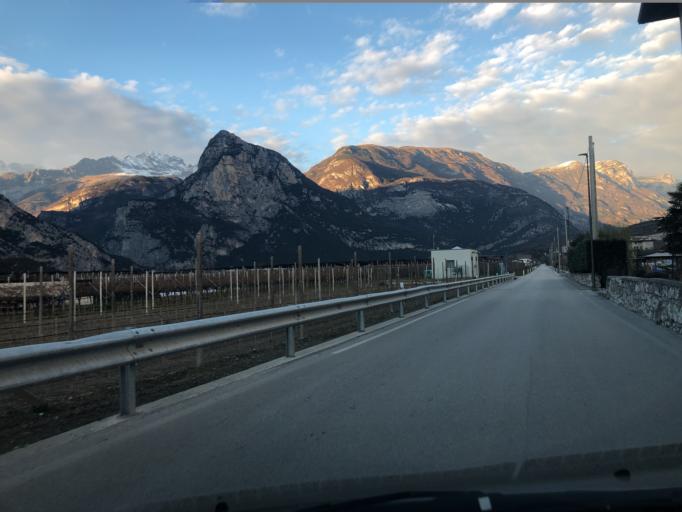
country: IT
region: Trentino-Alto Adige
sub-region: Provincia di Trento
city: Pietramurata
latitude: 46.0276
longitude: 10.9576
